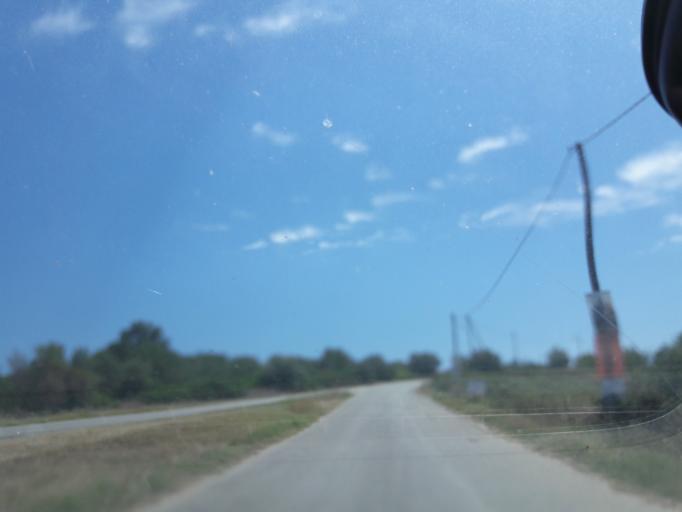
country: GR
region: Central Macedonia
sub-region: Nomos Chalkidikis
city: Nea Roda
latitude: 40.3290
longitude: 23.9227
